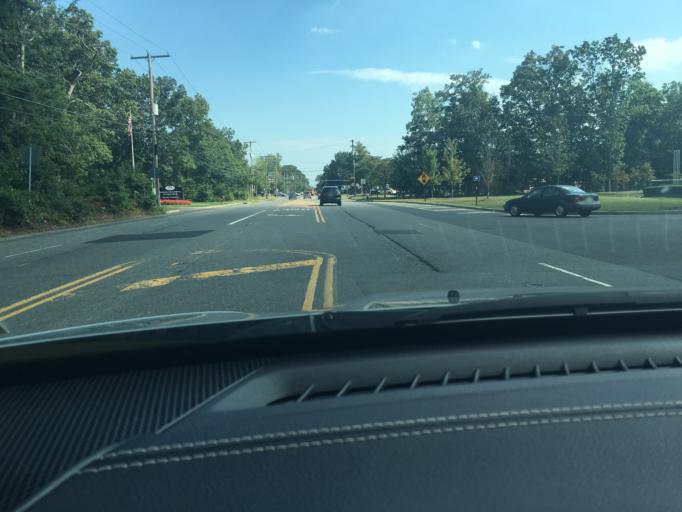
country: US
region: New Jersey
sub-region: Ocean County
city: Leisure Village West-Pine Lake Park
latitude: 40.0247
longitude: -74.2716
